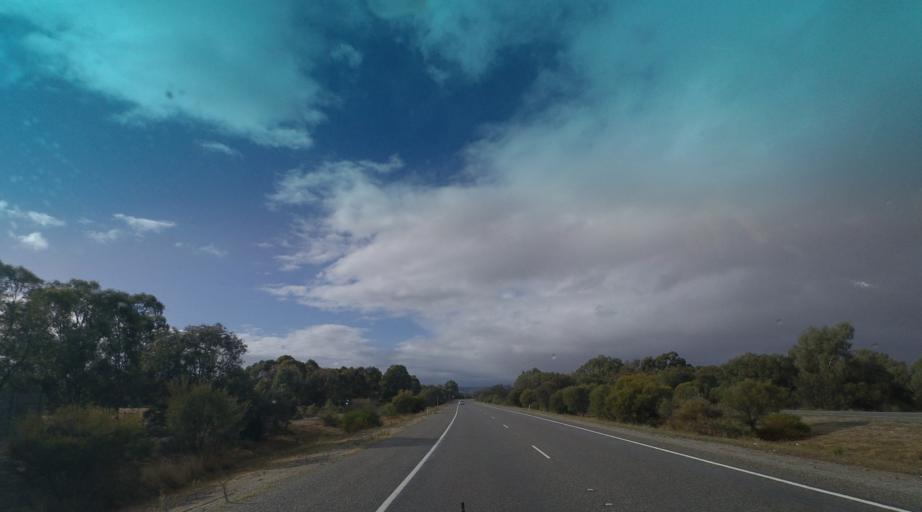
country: AU
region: Western Australia
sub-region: Serpentine-Jarrahdale
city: Oakford
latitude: -32.2019
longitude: 115.9655
